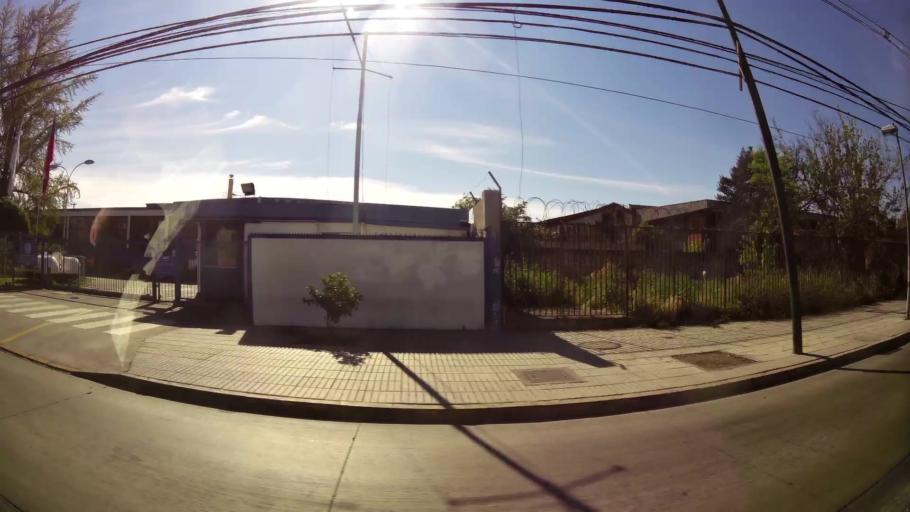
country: CL
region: Santiago Metropolitan
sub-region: Provincia de Santiago
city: Lo Prado
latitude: -33.5069
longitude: -70.7157
